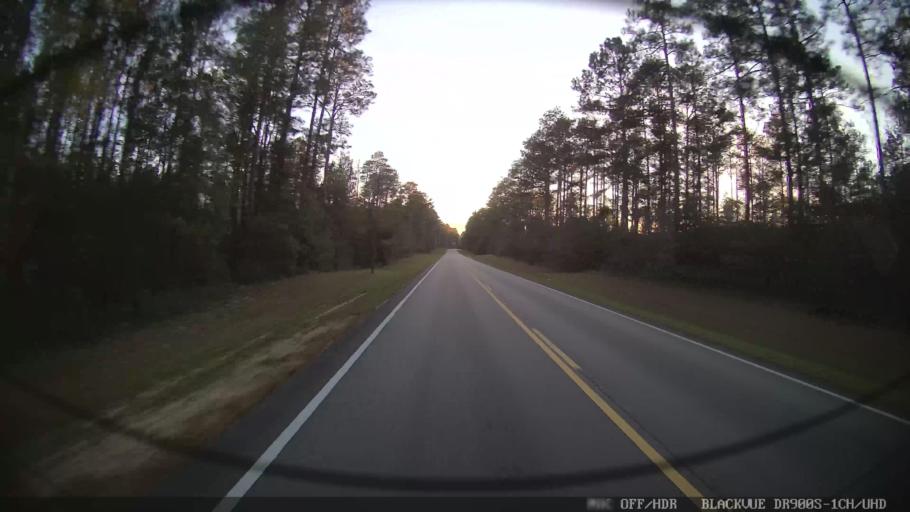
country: US
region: Mississippi
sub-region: Stone County
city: Wiggins
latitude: 31.0400
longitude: -89.2142
